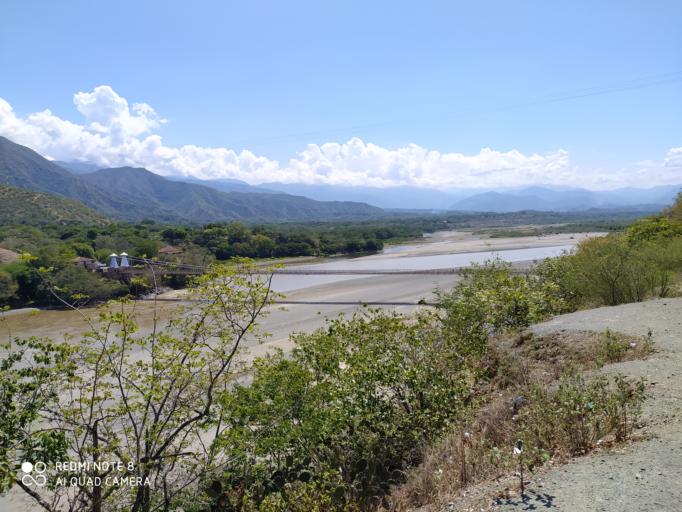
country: CO
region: Antioquia
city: Antioquia
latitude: 6.5799
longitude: -75.7999
